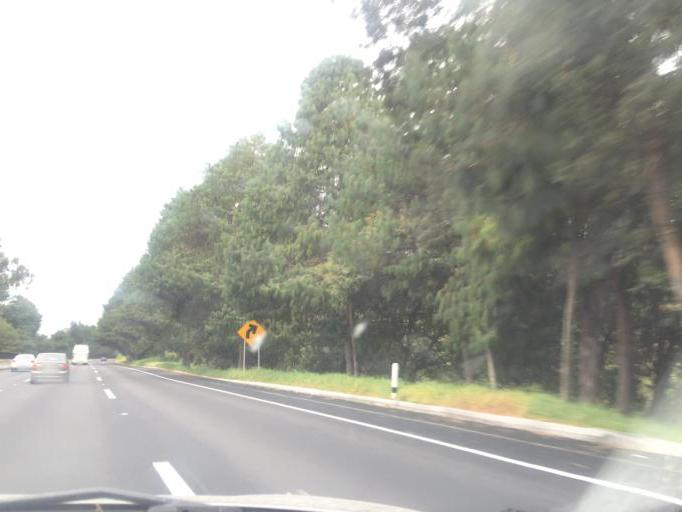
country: MX
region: Mexico City
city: Xochimilco
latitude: 19.1858
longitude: -99.1569
